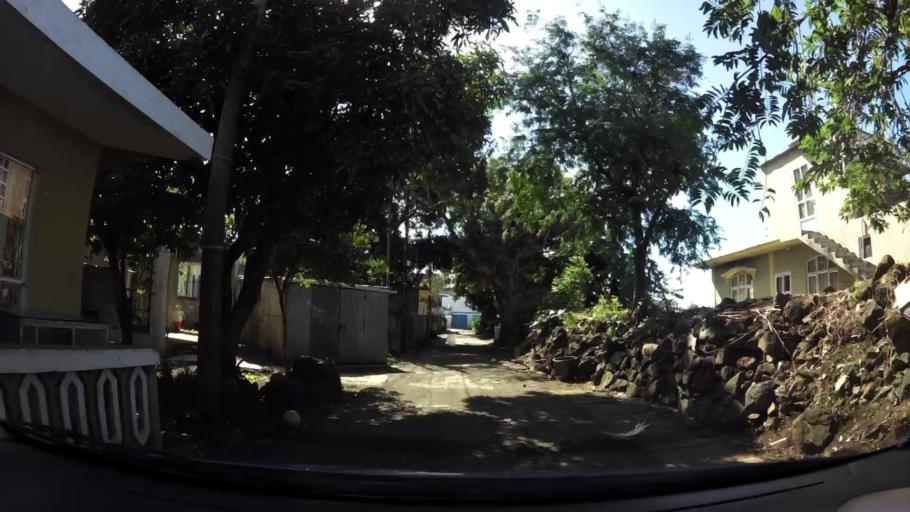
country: MU
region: Grand Port
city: Plaine Magnien
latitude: -20.4354
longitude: 57.6598
